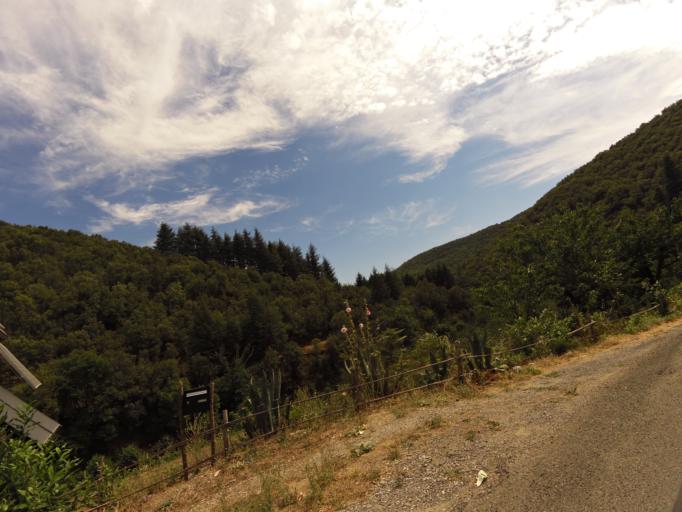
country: FR
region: Languedoc-Roussillon
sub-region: Departement du Gard
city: Le Vigan
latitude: 44.0145
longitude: 3.6458
